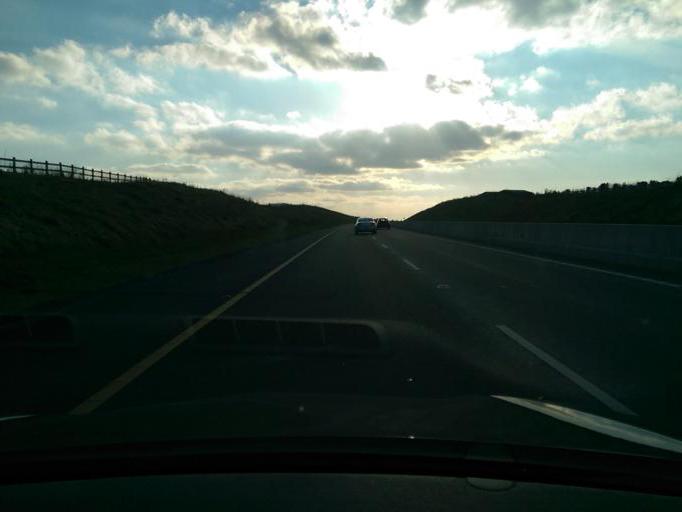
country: IE
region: Leinster
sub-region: Laois
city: Rathdowney
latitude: 52.9179
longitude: -7.6788
